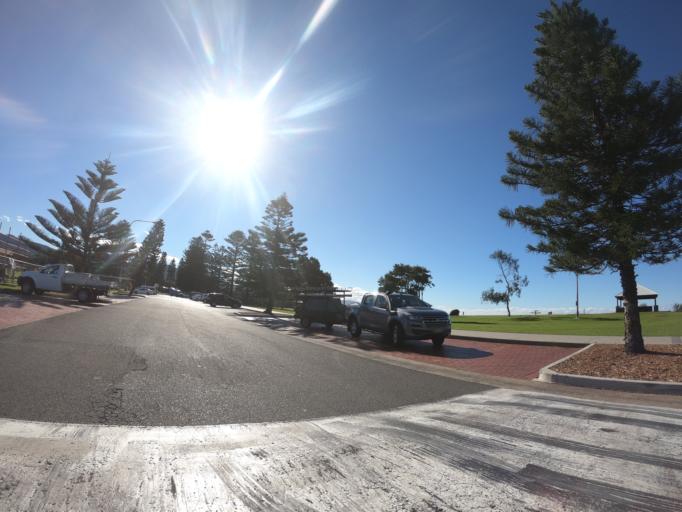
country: AU
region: New South Wales
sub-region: Wollongong
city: Gwynneville
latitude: -34.4108
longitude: 150.9009
